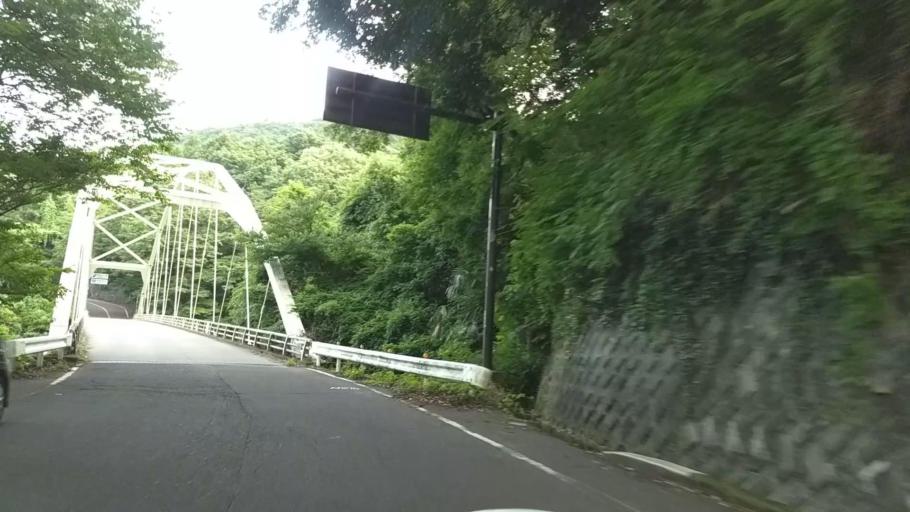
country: JP
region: Yamanashi
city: Uenohara
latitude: 35.6167
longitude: 139.1337
